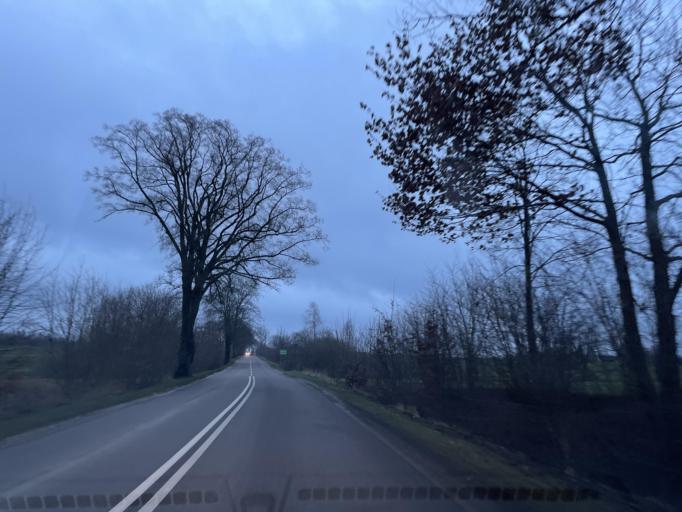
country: PL
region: Pomeranian Voivodeship
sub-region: Powiat wejherowski
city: Szemud
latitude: 54.4124
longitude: 18.2047
